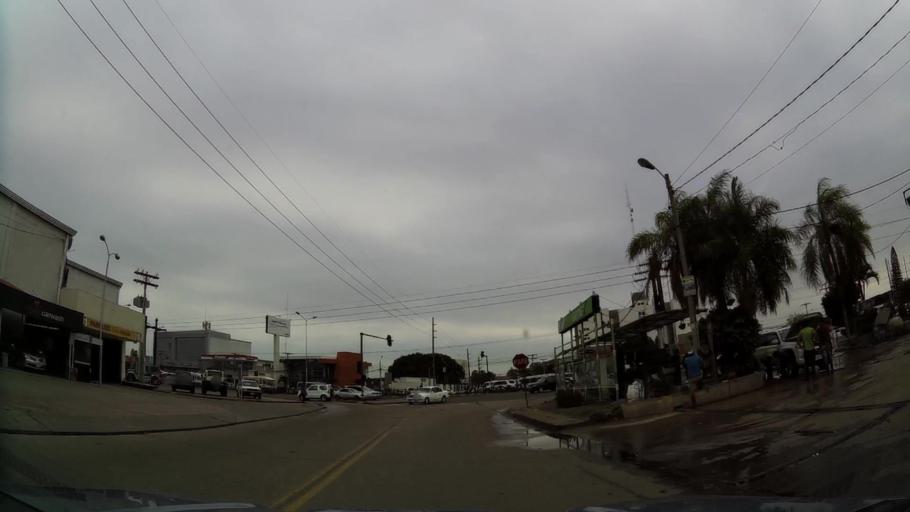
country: BO
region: Santa Cruz
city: Santa Cruz de la Sierra
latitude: -17.7580
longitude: -63.1779
